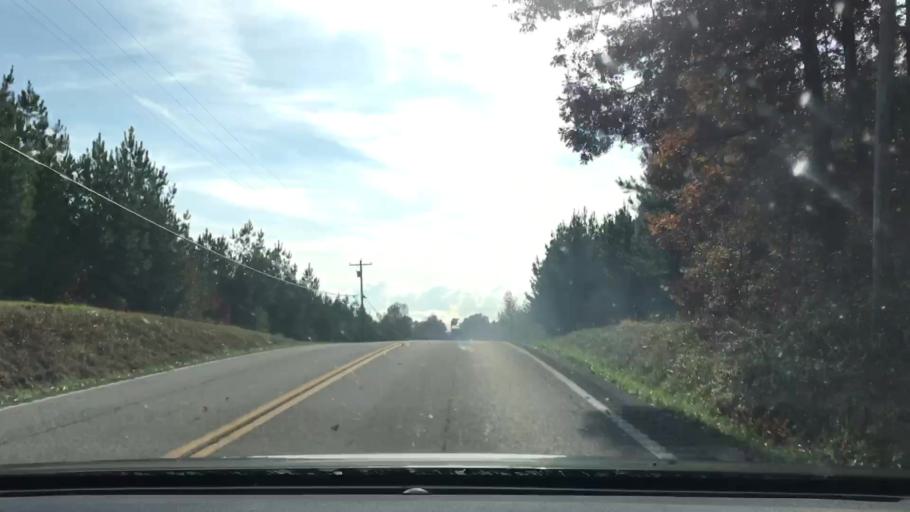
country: US
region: Tennessee
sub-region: Scott County
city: Huntsville
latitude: 36.3437
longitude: -84.6520
